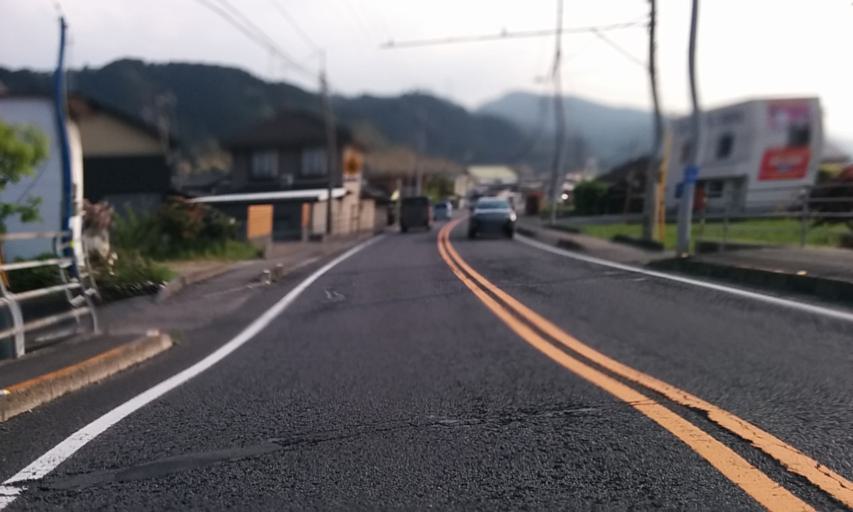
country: JP
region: Ehime
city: Saijo
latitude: 33.9010
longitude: 133.1823
